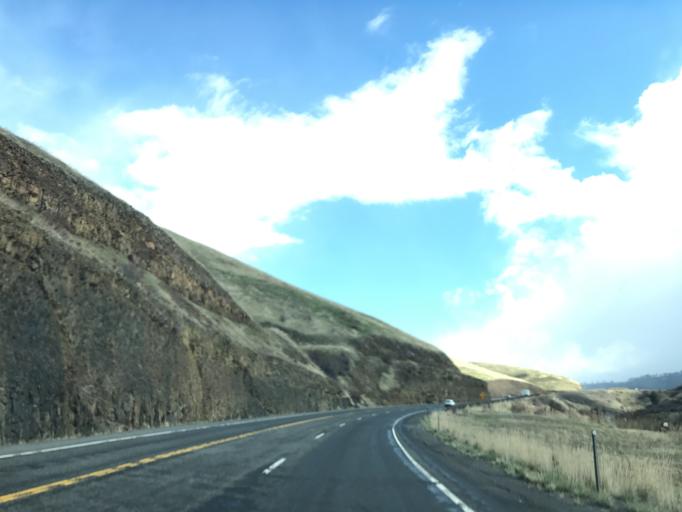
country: US
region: Idaho
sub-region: Idaho County
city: Grangeville
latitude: 45.8248
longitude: -116.2594
